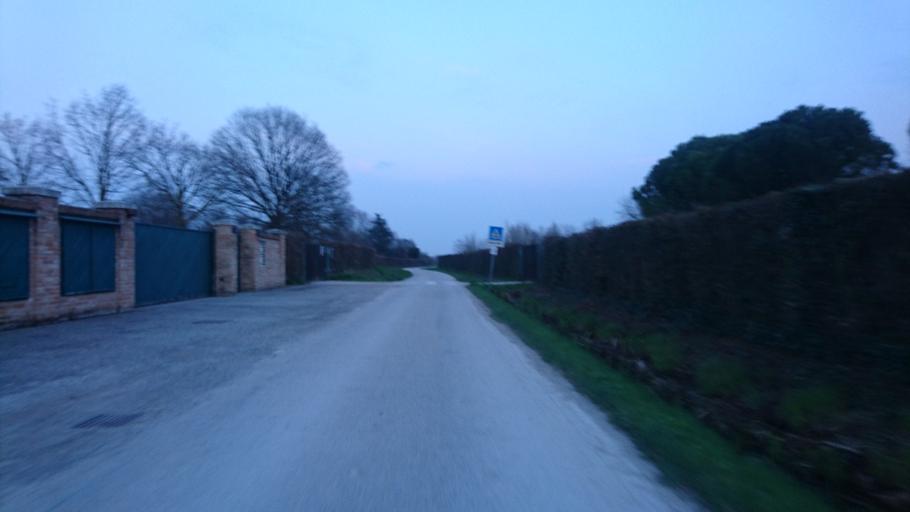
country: IT
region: Veneto
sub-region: Provincia di Padova
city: Saccolongo
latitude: 45.3869
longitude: 11.7513
